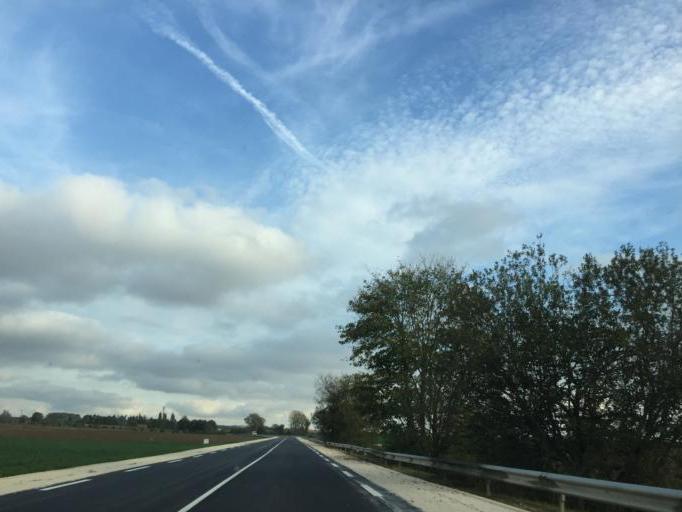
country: FR
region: Ile-de-France
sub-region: Departement de Seine-et-Marne
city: Jouy-le-Chatel
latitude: 48.6888
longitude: 3.0938
